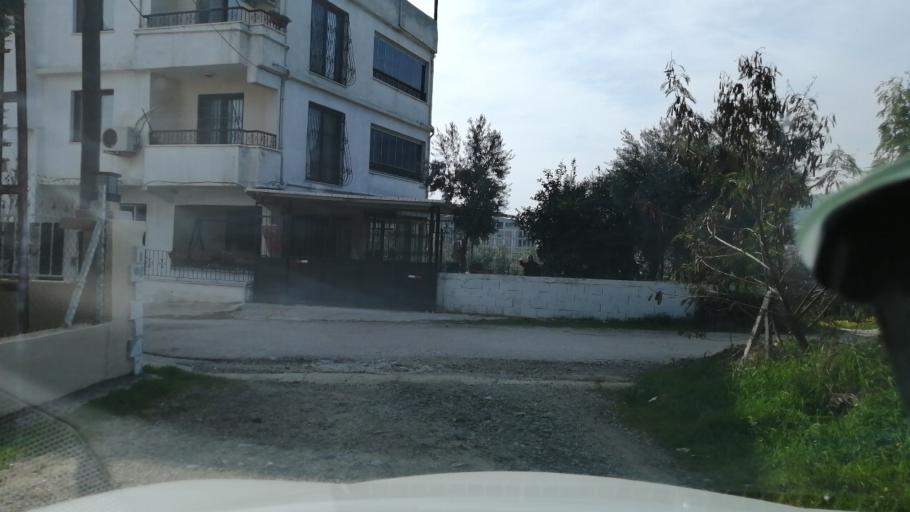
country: TR
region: Hatay
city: Serinyol
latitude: 36.3536
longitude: 36.2048
